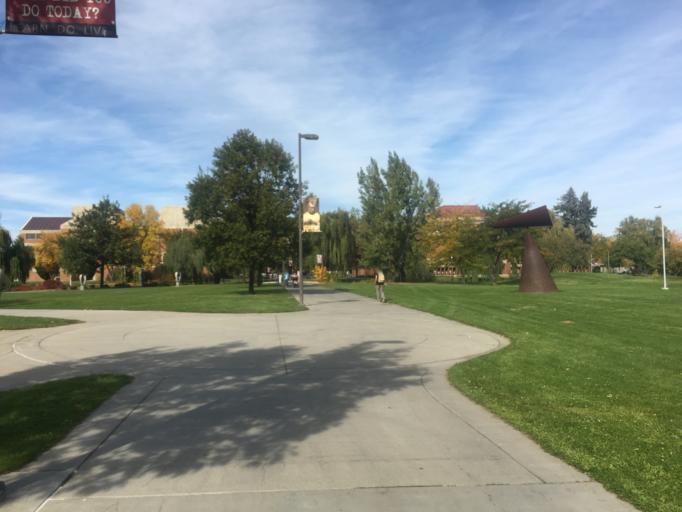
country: US
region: Washington
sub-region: Kittitas County
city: Ellensburg
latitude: 47.0034
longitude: -120.5408
